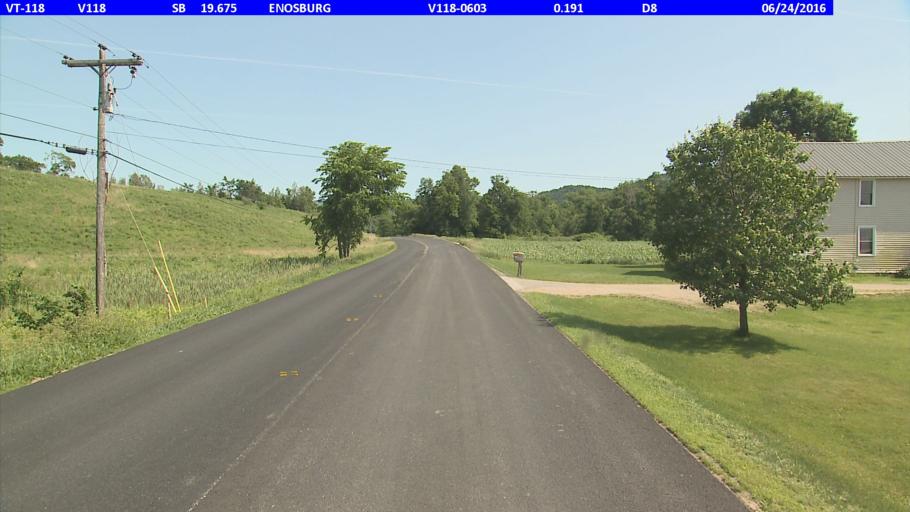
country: US
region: Vermont
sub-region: Franklin County
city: Richford
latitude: 44.9229
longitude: -72.6748
